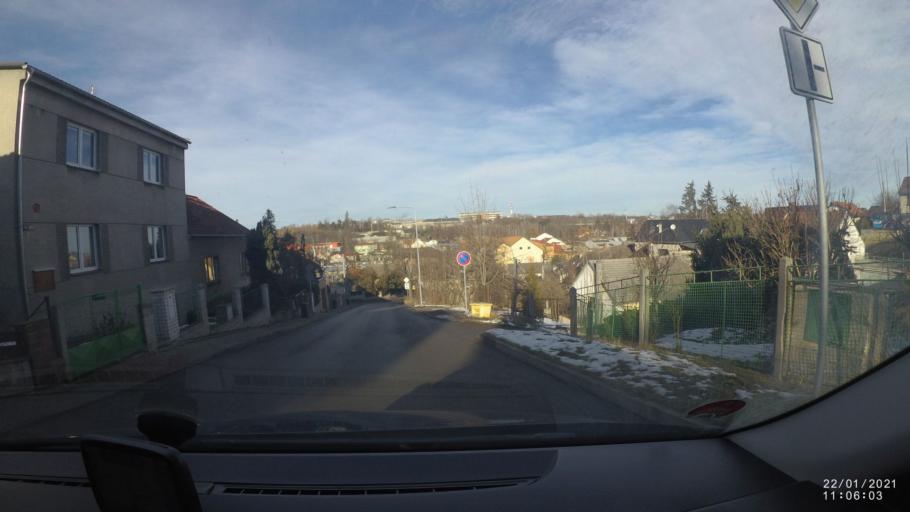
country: CZ
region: Central Bohemia
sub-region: Okres Beroun
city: Horovice
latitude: 49.8357
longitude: 13.8992
